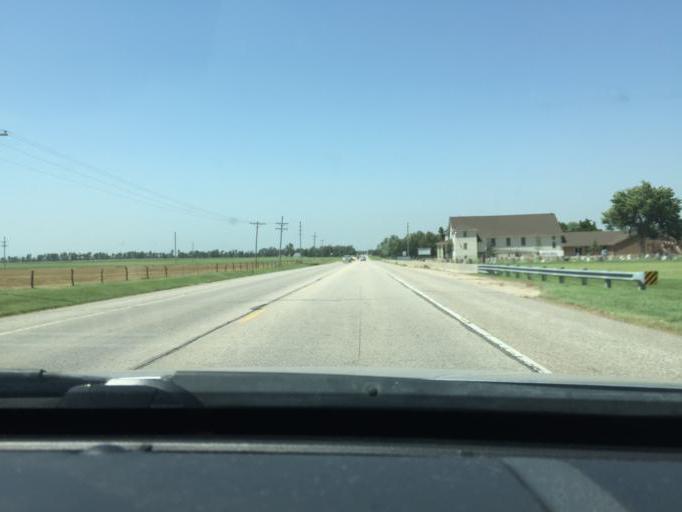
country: US
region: Kansas
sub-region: Reno County
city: Haven
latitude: 37.9534
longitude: -97.8668
